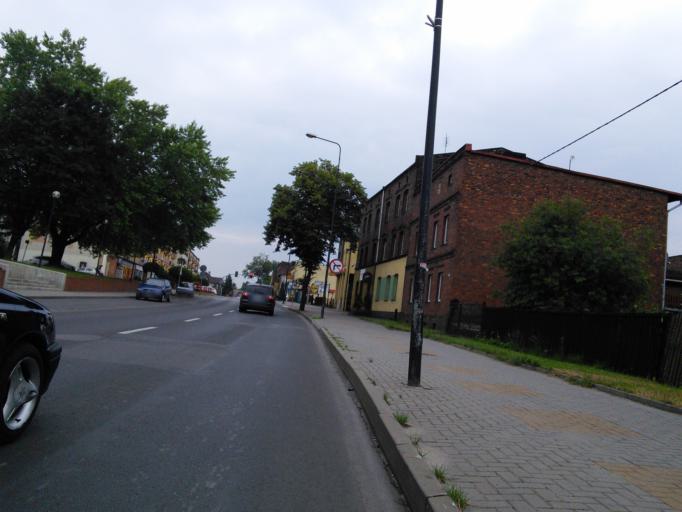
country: PL
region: Silesian Voivodeship
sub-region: Piekary Slaskie
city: Brzeziny Slaskie
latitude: 50.3676
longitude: 18.9788
